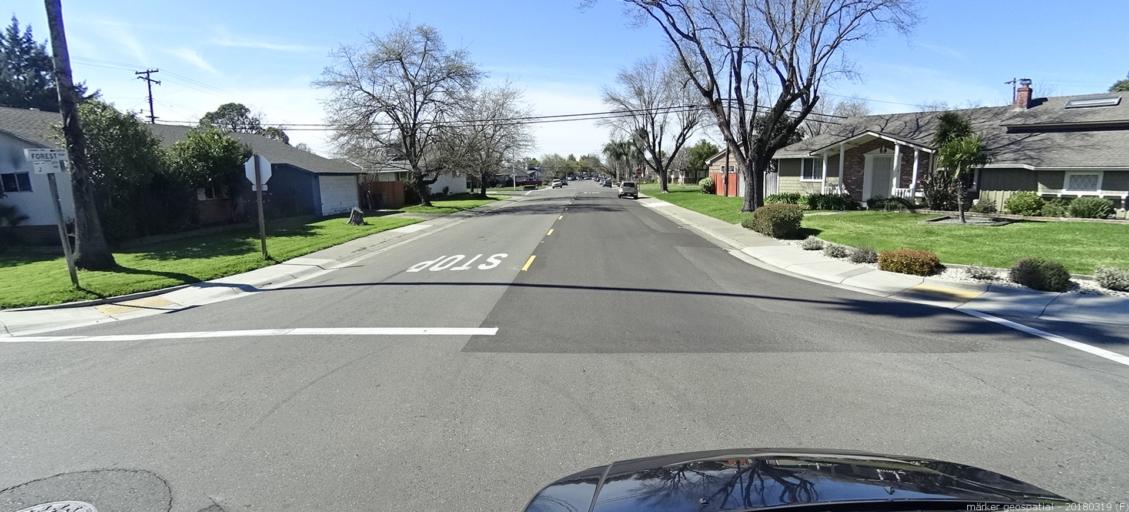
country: US
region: California
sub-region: Sacramento County
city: Parkway
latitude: 38.4926
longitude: -121.4452
